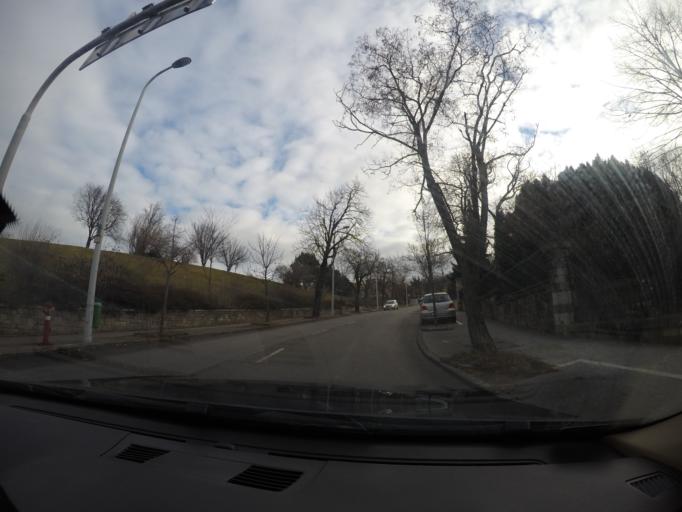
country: HU
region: Budapest
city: Budapest I. keruelet
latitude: 47.4894
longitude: 19.0371
